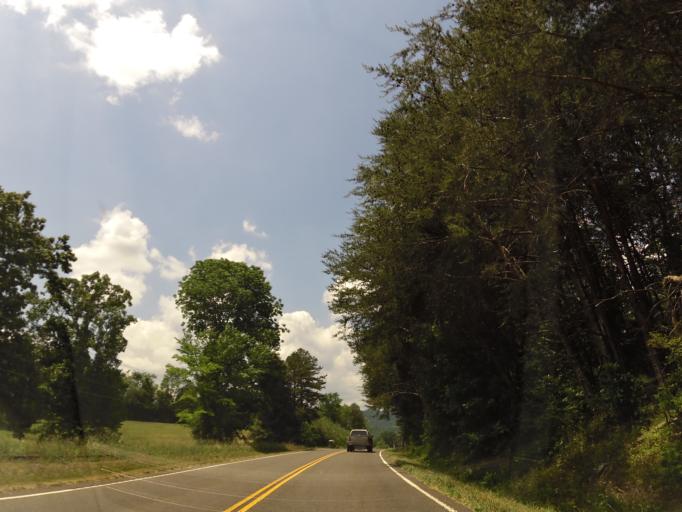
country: US
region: Tennessee
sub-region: Rhea County
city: Spring City
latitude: 35.6527
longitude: -84.8809
